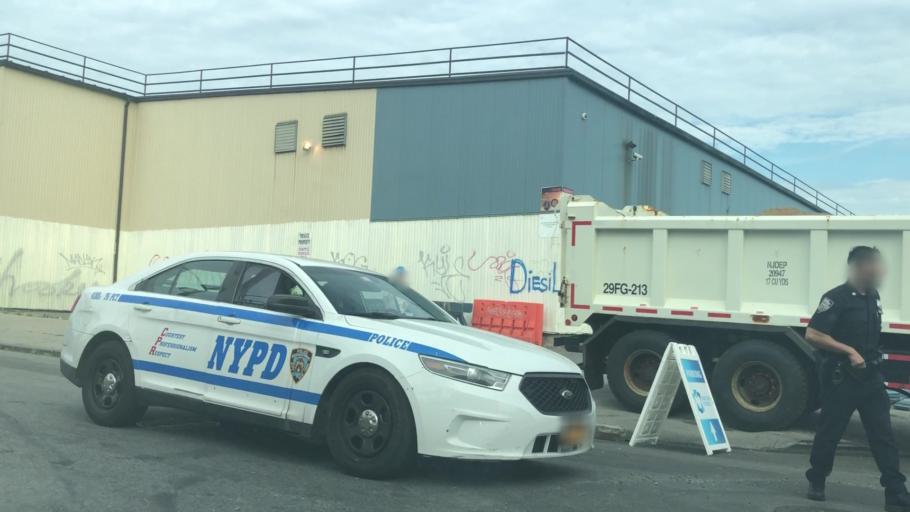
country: US
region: New York
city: New York City
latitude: 40.6791
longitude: -74.0156
